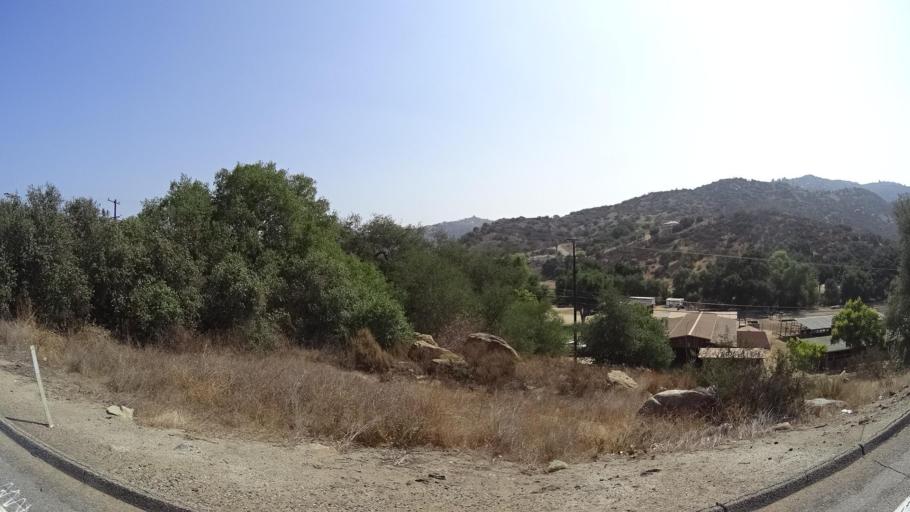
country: US
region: California
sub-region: San Diego County
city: Hidden Meadows
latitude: 33.2465
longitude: -117.1505
